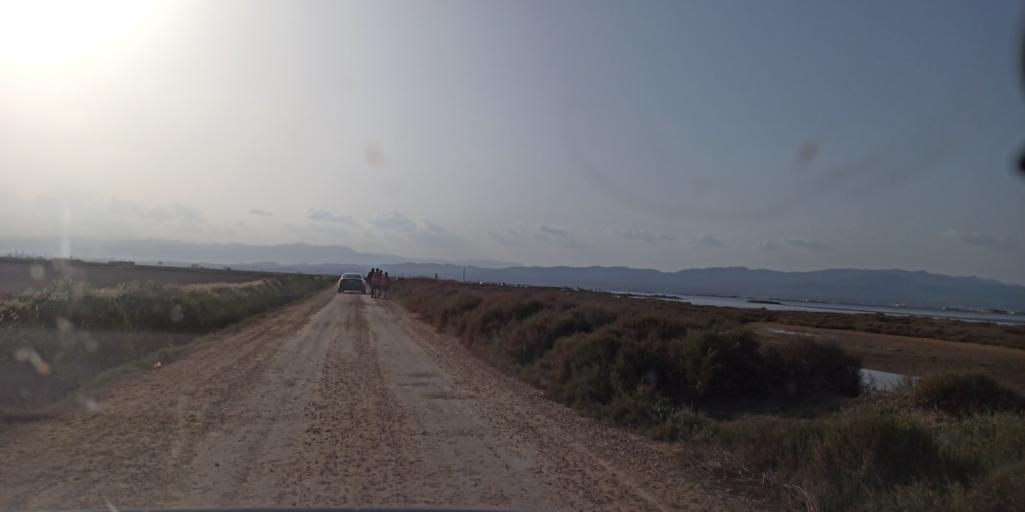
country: ES
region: Catalonia
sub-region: Provincia de Tarragona
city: Deltebre
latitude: 40.7631
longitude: 0.7535
